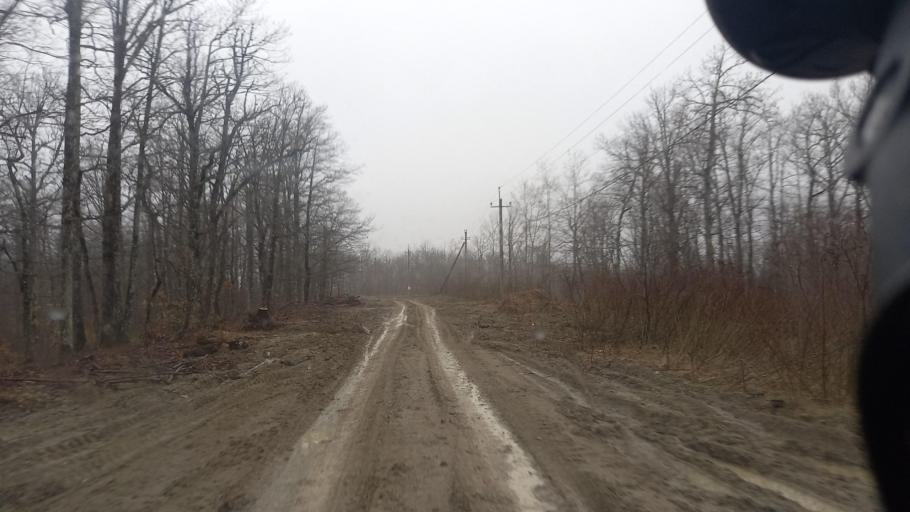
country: RU
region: Krasnodarskiy
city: Saratovskaya
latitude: 44.6162
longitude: 39.2361
